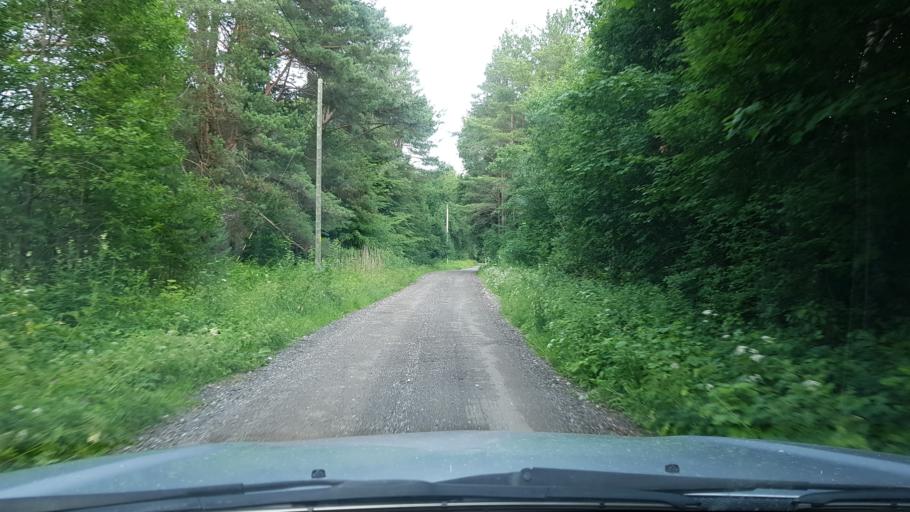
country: EE
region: Ida-Virumaa
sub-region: Narva-Joesuu linn
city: Narva-Joesuu
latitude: 59.4573
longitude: 28.0674
